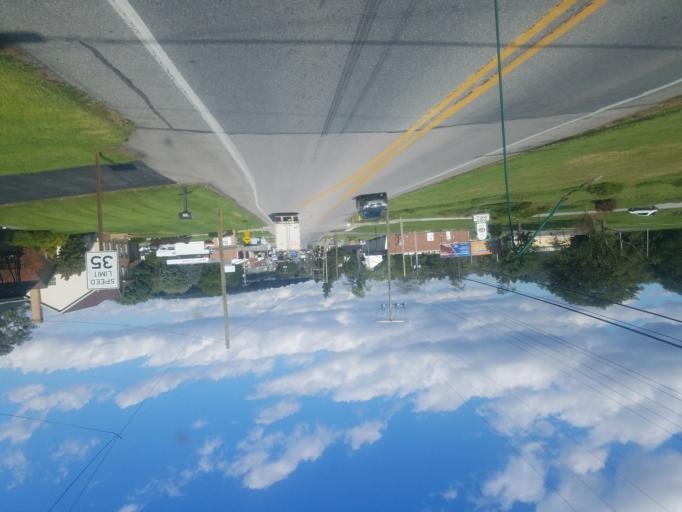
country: US
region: Pennsylvania
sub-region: York County
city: Emigsville
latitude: 40.0119
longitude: -76.7312
